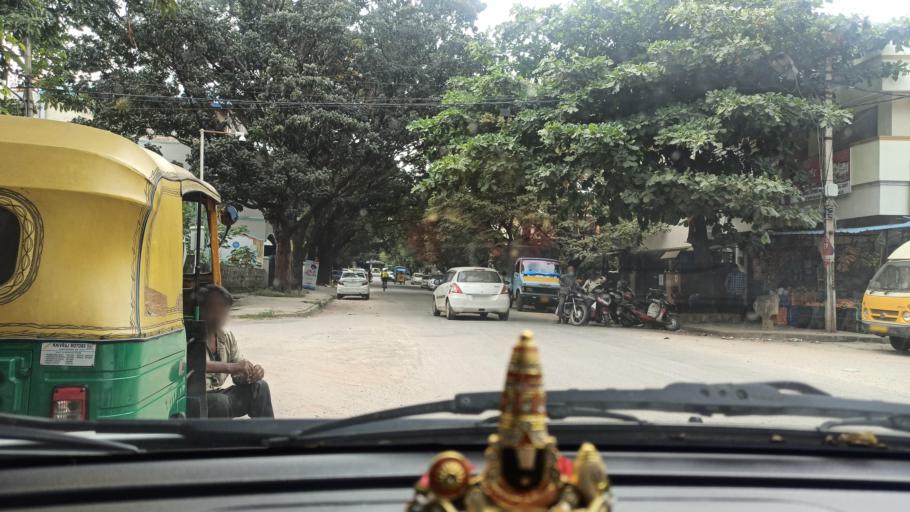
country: IN
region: Karnataka
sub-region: Bangalore Urban
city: Bangalore
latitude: 13.0177
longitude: 77.6452
